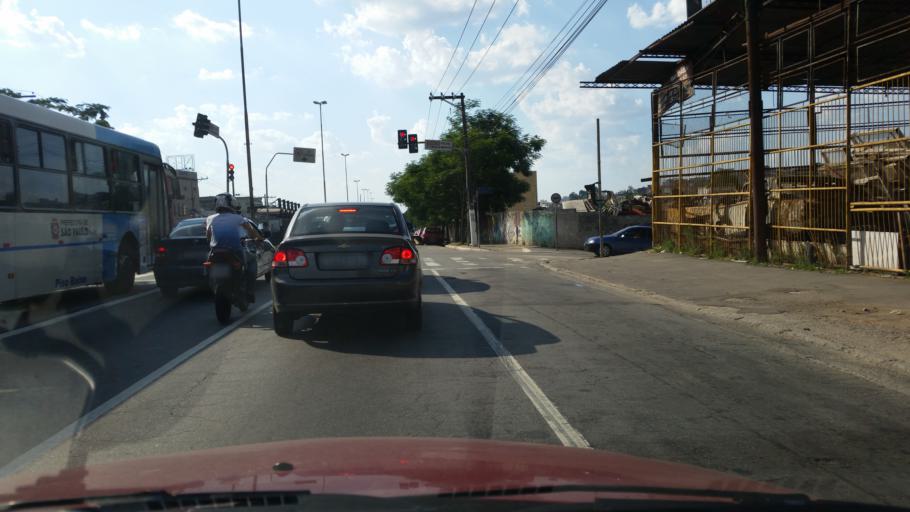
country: BR
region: Sao Paulo
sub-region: Diadema
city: Diadema
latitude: -23.6727
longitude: -46.6443
